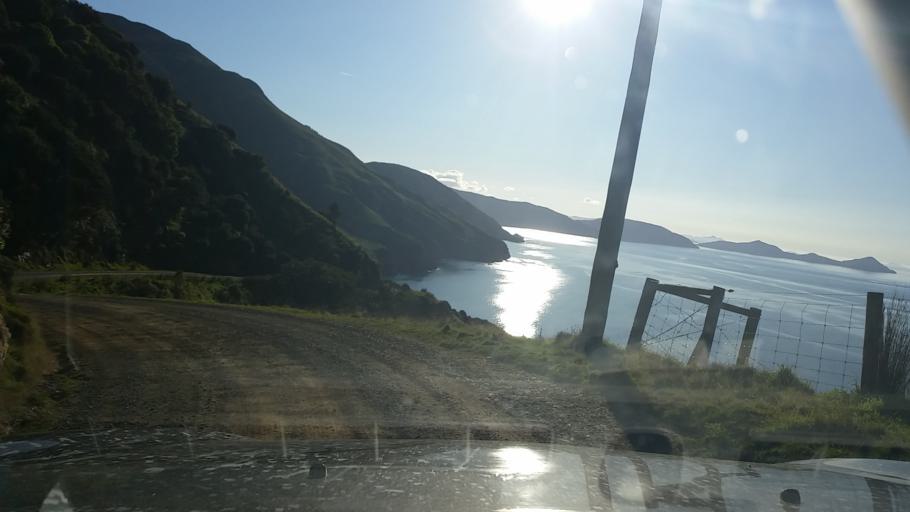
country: NZ
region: Marlborough
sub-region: Marlborough District
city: Picton
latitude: -41.0227
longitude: 174.1442
